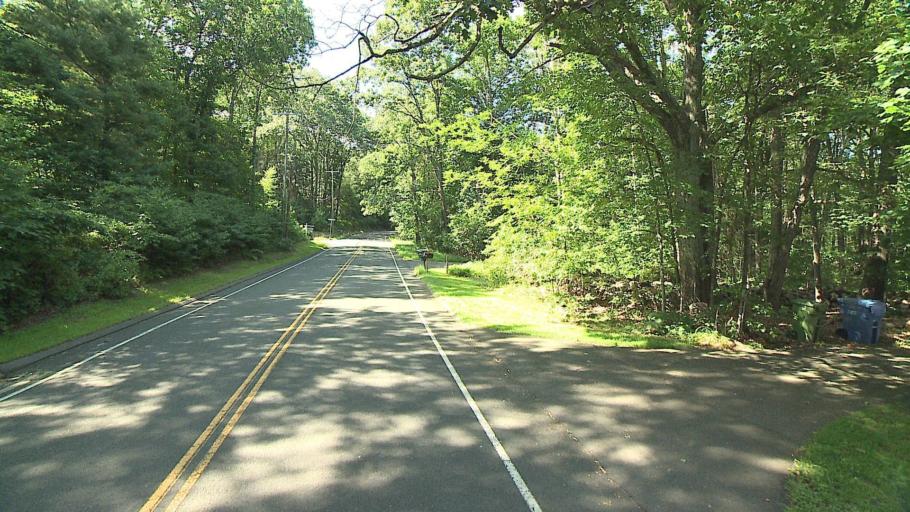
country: US
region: Connecticut
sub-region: Hartford County
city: West Simsbury
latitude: 41.8845
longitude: -72.8753
